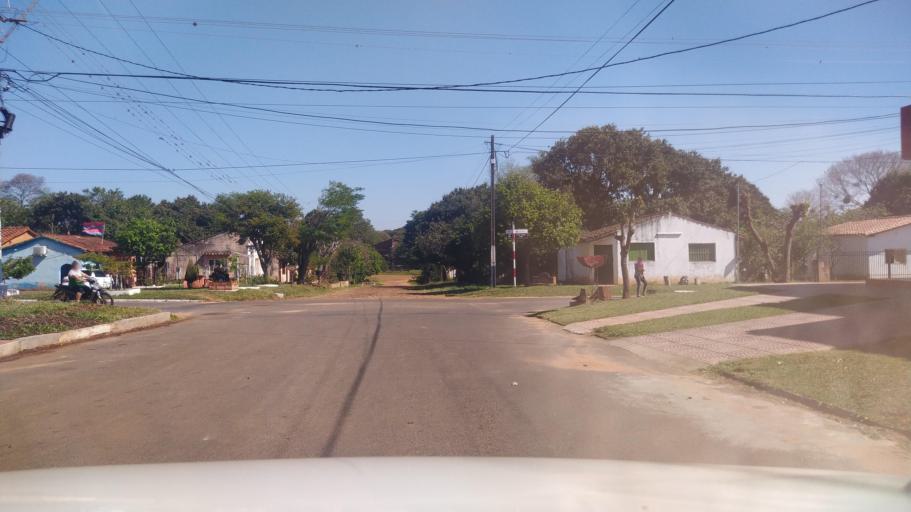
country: PY
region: Misiones
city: San Juan Bautista
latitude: -26.6656
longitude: -57.1506
